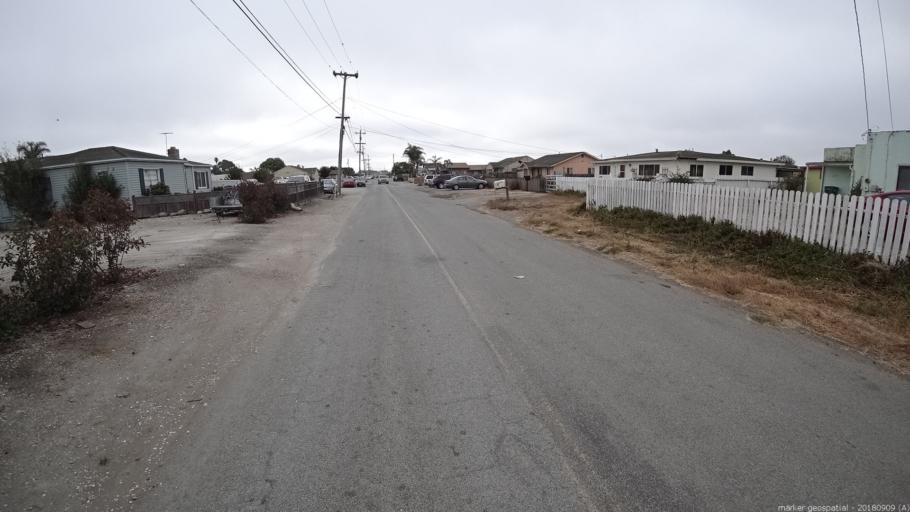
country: US
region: California
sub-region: Monterey County
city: Boronda
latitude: 36.7009
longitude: -121.6768
